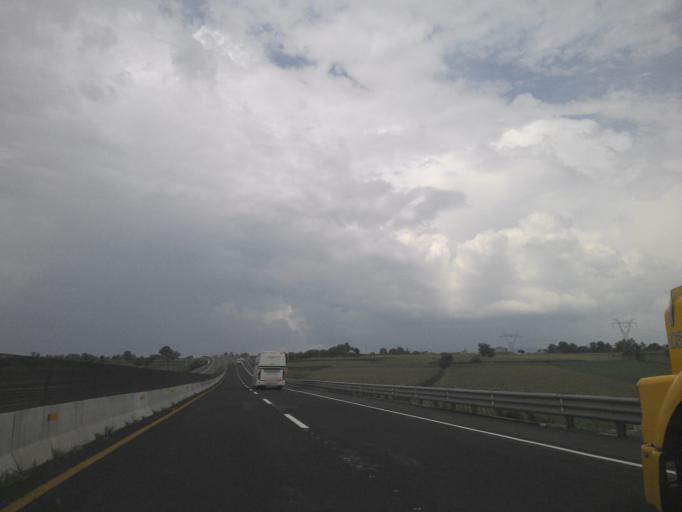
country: MX
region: Hidalgo
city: San Marcos
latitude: 20.0837
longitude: -99.3309
